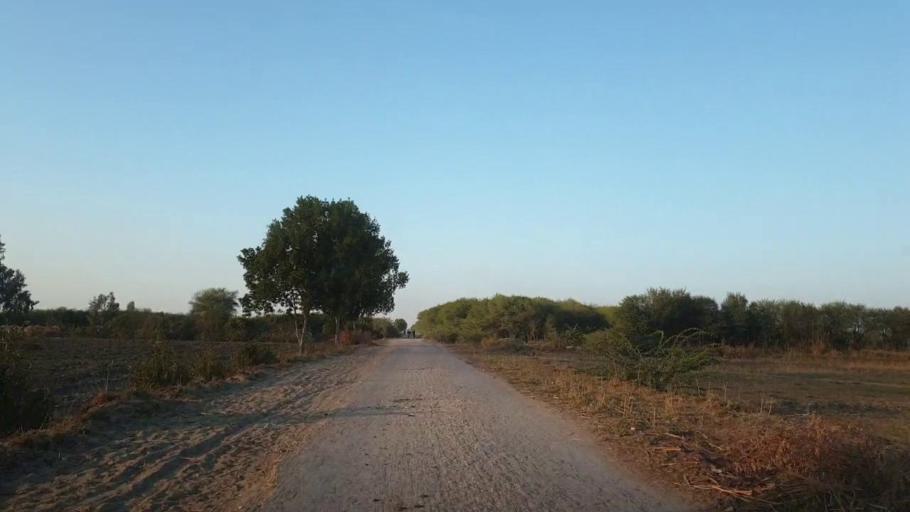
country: PK
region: Sindh
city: Mirpur Khas
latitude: 25.6655
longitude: 69.0482
